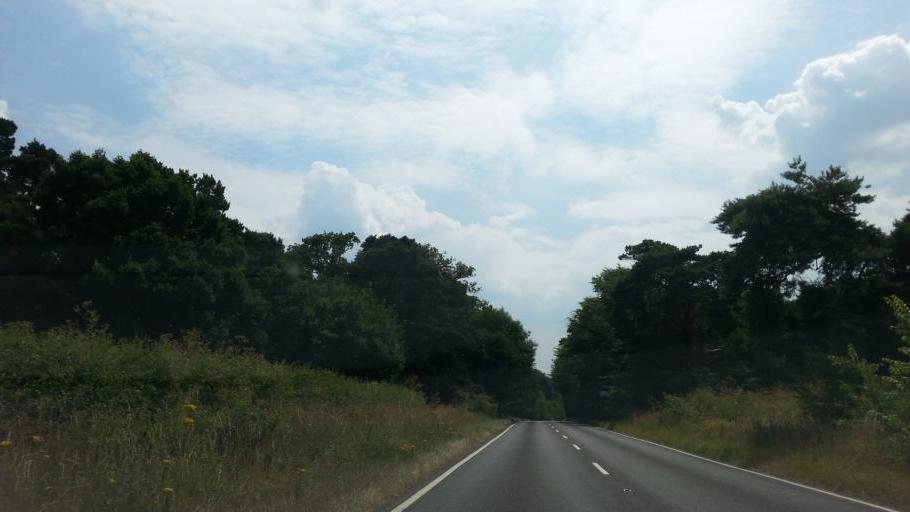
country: GB
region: England
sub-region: Suffolk
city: Lakenheath
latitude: 52.3668
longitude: 0.5401
